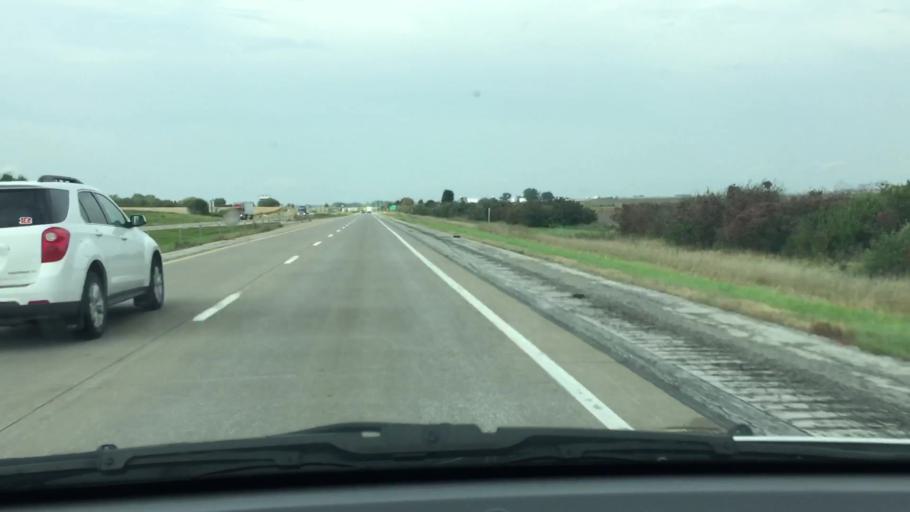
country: US
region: Iowa
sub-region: Cedar County
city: Durant
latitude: 41.6331
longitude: -90.8460
